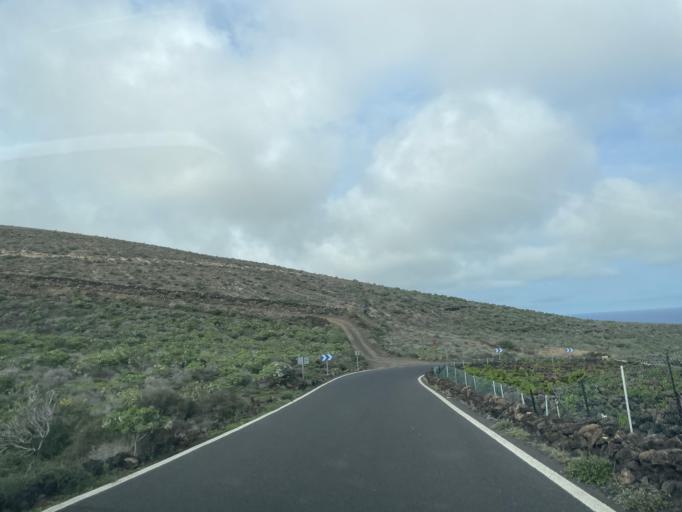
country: ES
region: Canary Islands
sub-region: Provincia de Las Palmas
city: Haria
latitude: 29.1967
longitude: -13.4588
